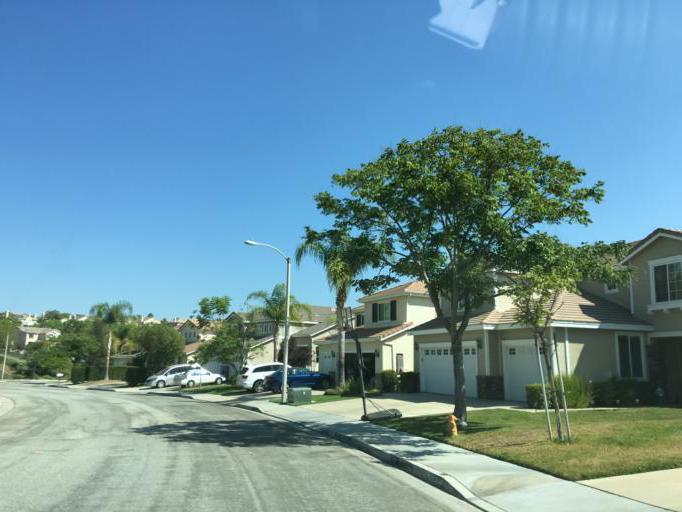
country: US
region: California
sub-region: Los Angeles County
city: Santa Clarita
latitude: 34.3918
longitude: -118.5904
